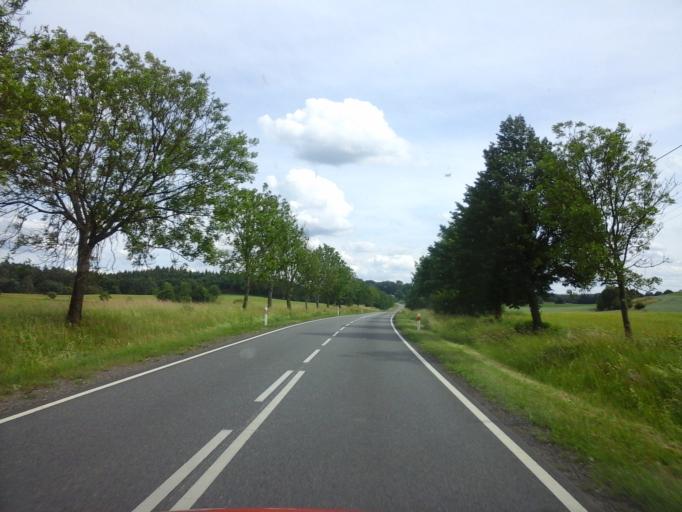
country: PL
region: West Pomeranian Voivodeship
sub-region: Powiat lobeski
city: Wegorzyno
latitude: 53.5212
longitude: 15.5688
